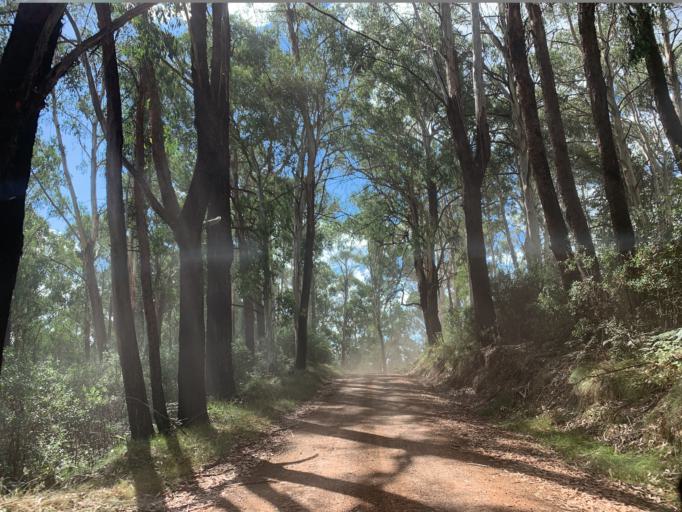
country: AU
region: Victoria
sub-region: Mansfield
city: Mansfield
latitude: -37.0919
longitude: 146.5416
